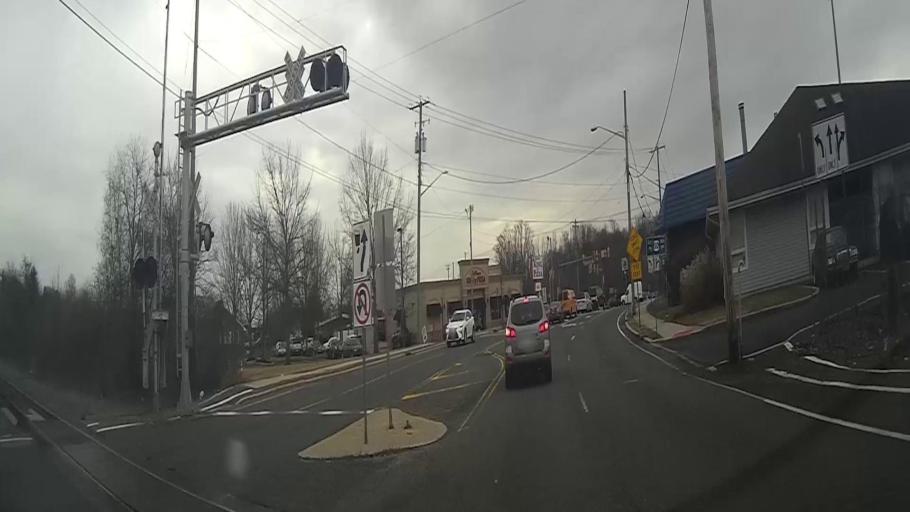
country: US
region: New Jersey
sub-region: Camden County
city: Berlin
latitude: 39.7981
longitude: -74.9327
